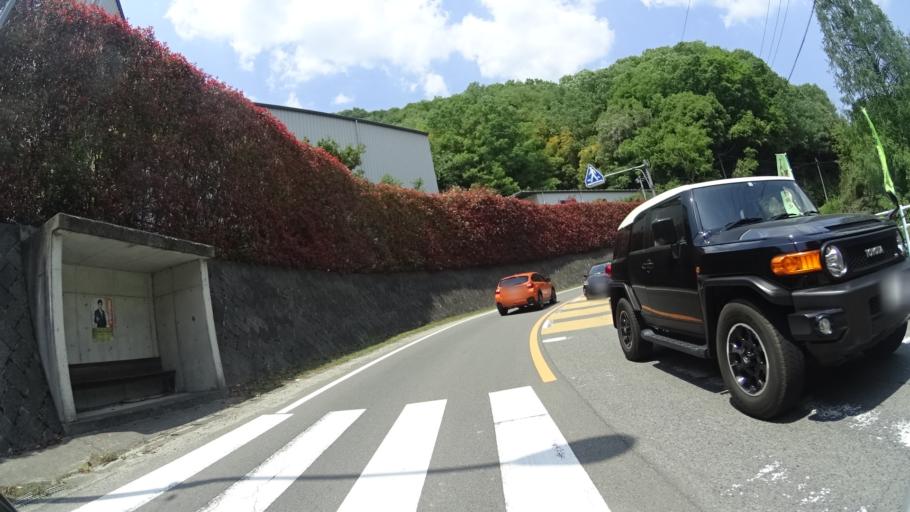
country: JP
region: Ehime
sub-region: Shikoku-chuo Shi
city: Matsuyama
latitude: 33.8853
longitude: 132.8347
